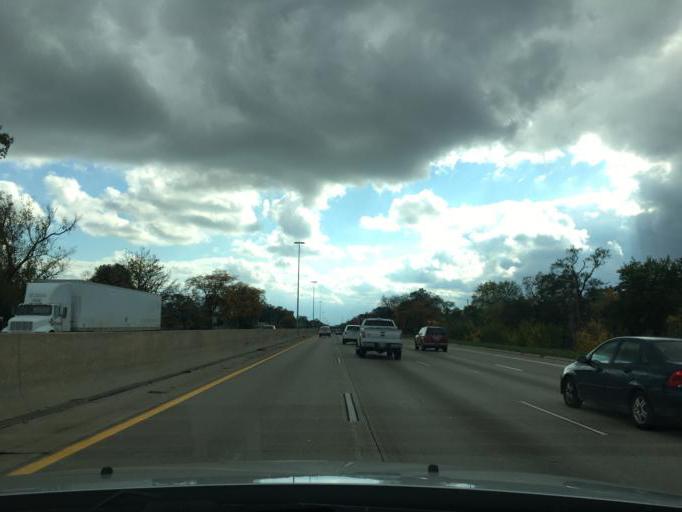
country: US
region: Michigan
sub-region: Oakland County
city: Southfield
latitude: 42.4270
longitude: -83.2193
